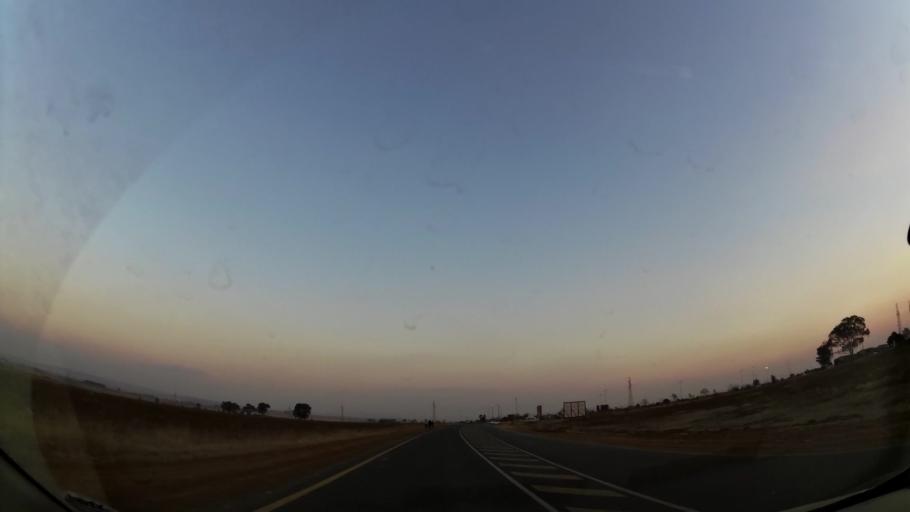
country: ZA
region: Gauteng
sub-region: Ekurhuleni Metropolitan Municipality
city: Nigel
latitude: -26.3747
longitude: 28.4214
